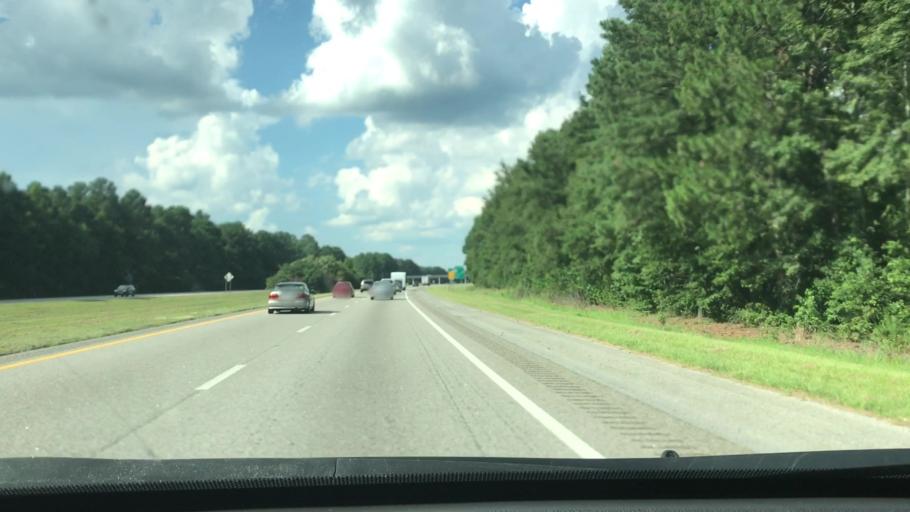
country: US
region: South Carolina
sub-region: Sumter County
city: East Sumter
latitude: 33.8952
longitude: -80.0961
